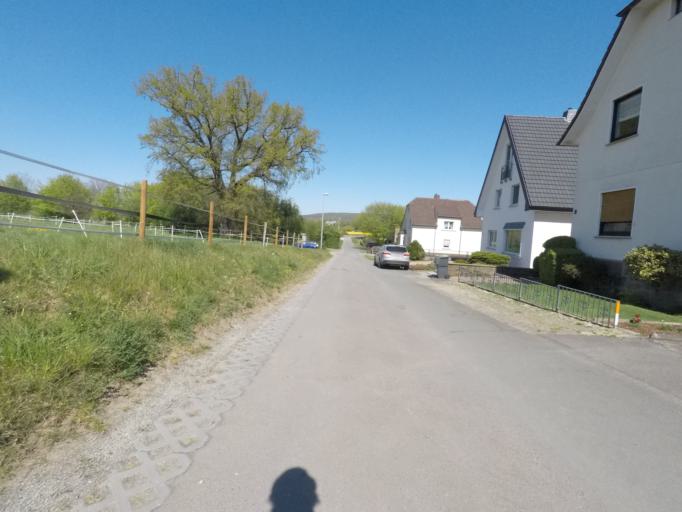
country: DE
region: North Rhine-Westphalia
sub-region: Regierungsbezirk Detmold
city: Herford
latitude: 52.0891
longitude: 8.7013
